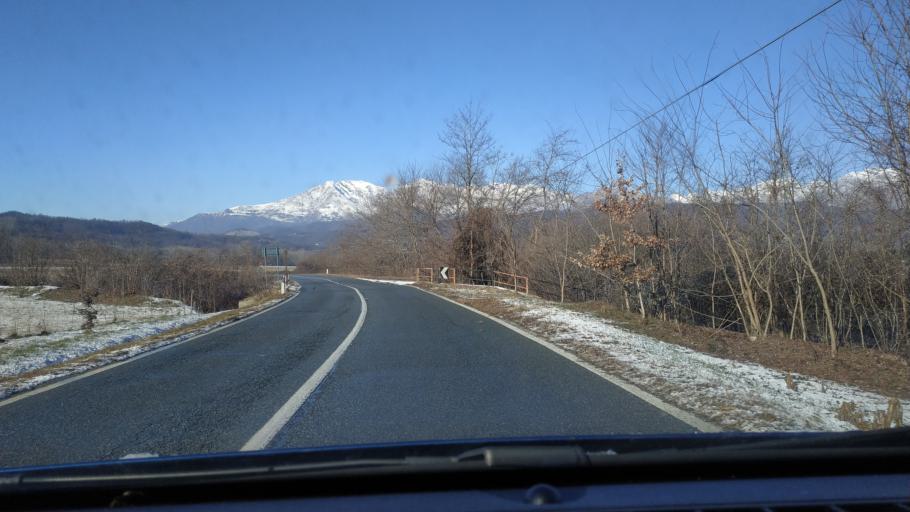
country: IT
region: Piedmont
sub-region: Provincia di Torino
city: Perosa Canavese
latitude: 45.4104
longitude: 7.8253
